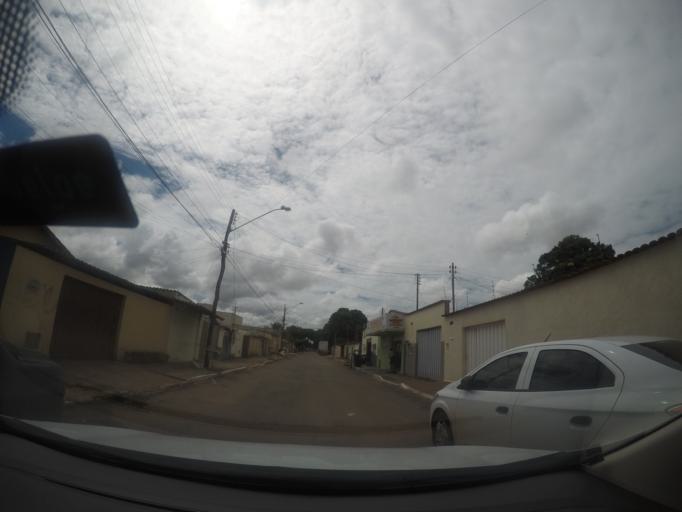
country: BR
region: Goias
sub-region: Goiania
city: Goiania
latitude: -16.6572
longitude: -49.3002
